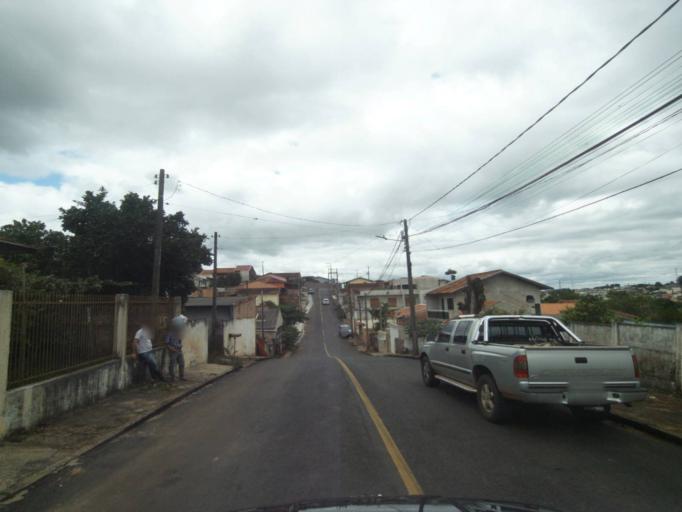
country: BR
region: Parana
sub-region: Telemaco Borba
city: Telemaco Borba
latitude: -24.3252
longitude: -50.6388
